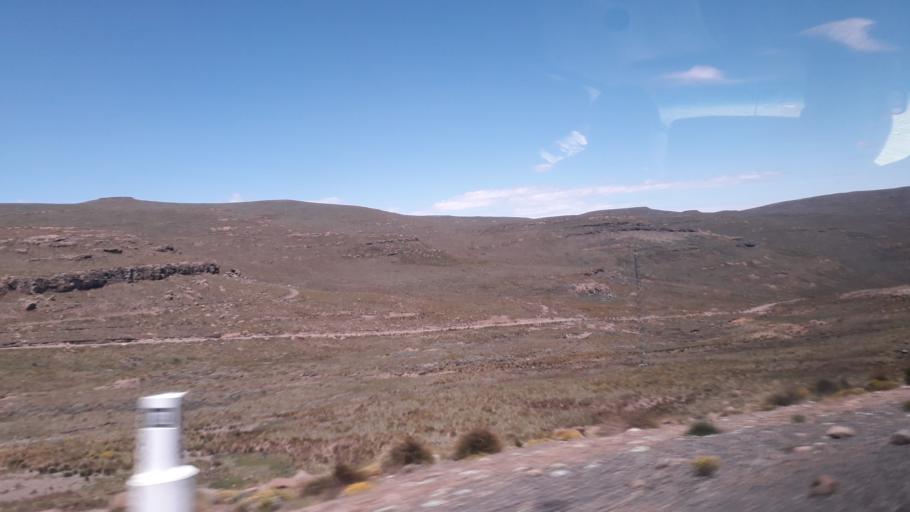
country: ZA
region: Orange Free State
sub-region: Thabo Mofutsanyana District Municipality
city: Phuthaditjhaba
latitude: -28.8095
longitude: 28.7100
